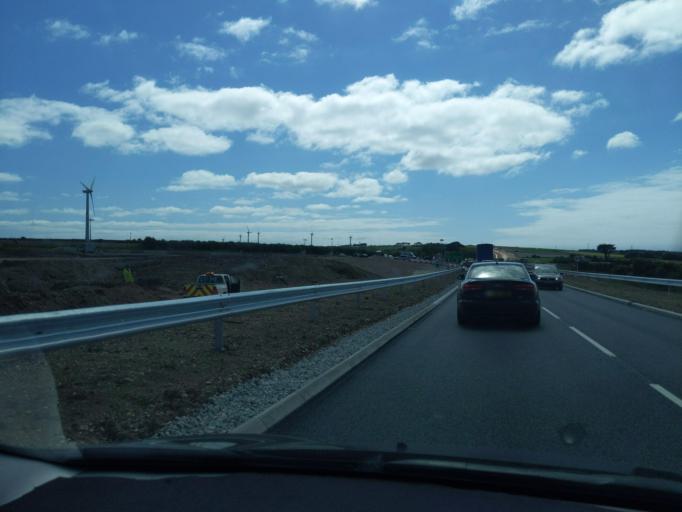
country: GB
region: England
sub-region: Cornwall
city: Perranporth
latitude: 50.2979
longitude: -5.1218
